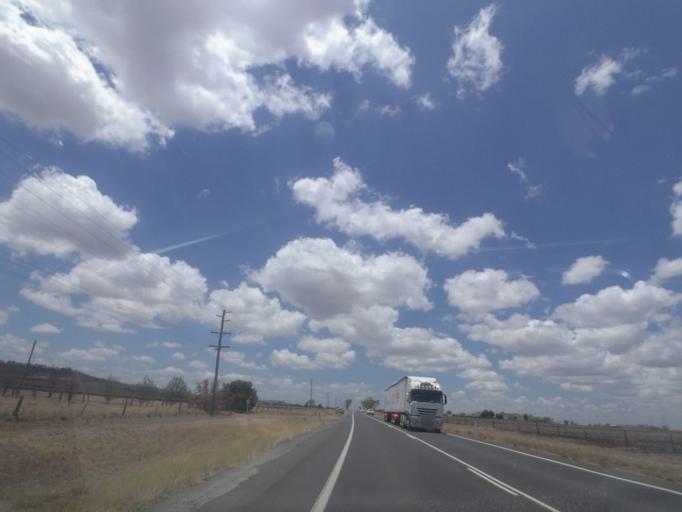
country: AU
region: Queensland
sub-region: Toowoomba
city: Top Camp
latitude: -27.7348
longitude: 151.9142
